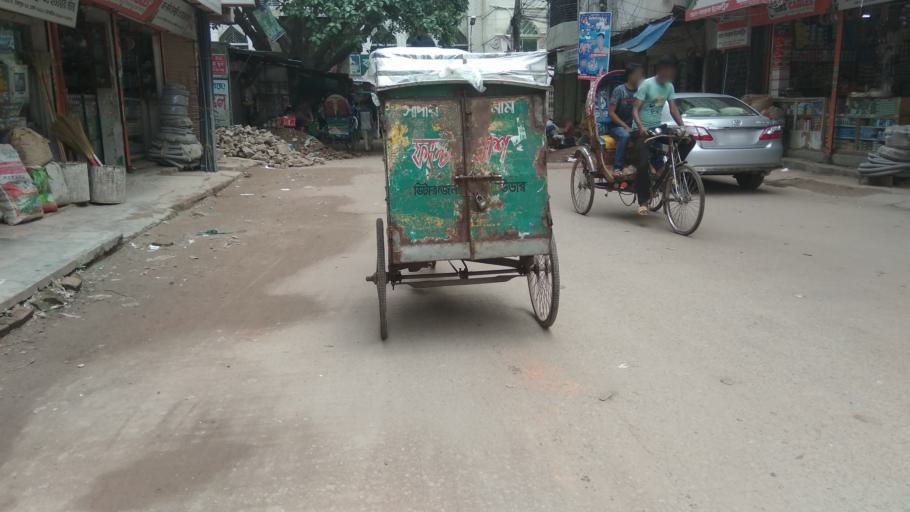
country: BD
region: Dhaka
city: Azimpur
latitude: 23.8129
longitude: 90.3694
